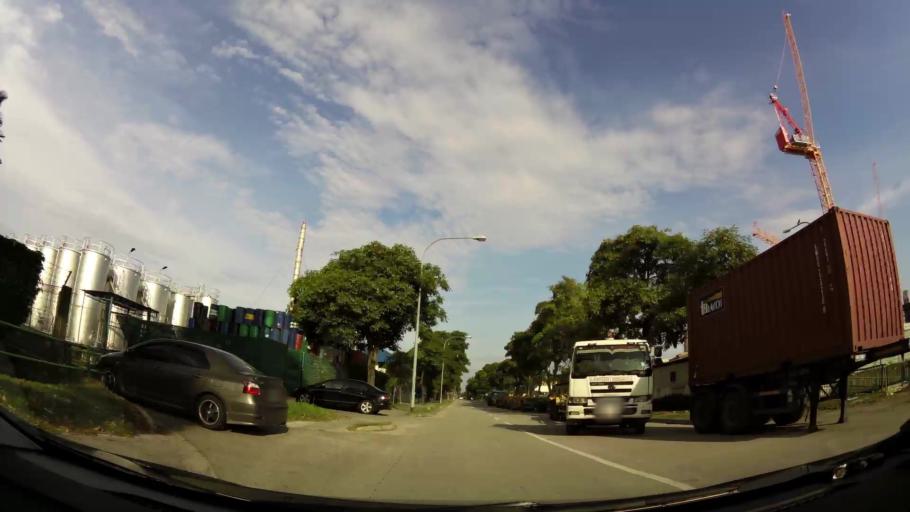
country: MY
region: Johor
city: Johor Bahru
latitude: 1.3242
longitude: 103.6583
